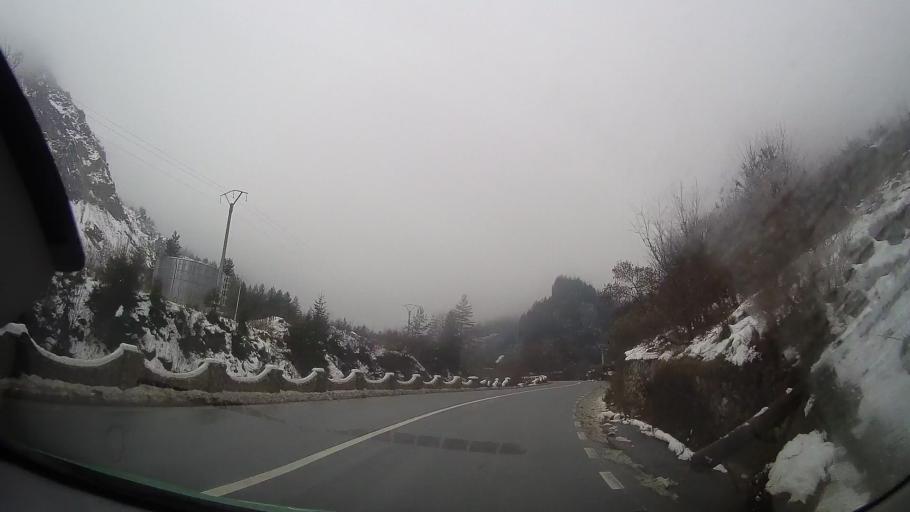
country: RO
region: Neamt
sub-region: Comuna Bicaz Chei
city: Bicaz Chei
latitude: 46.8239
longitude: 25.8561
